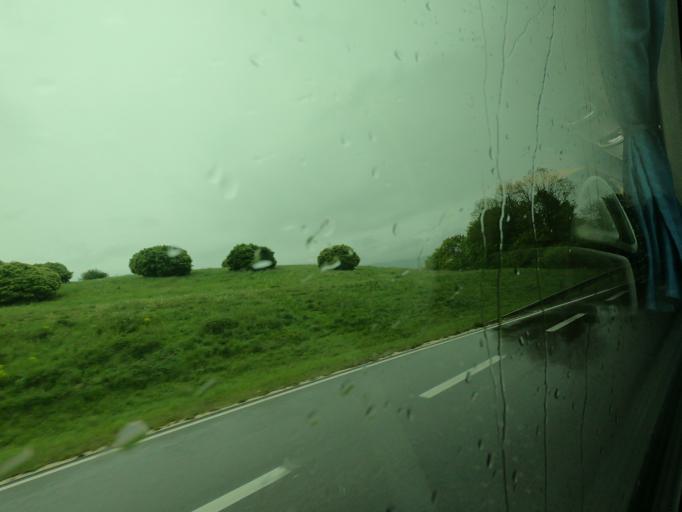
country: DE
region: Baden-Wuerttemberg
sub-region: Regierungsbezirk Stuttgart
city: Aalen
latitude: 48.8275
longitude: 10.0745
